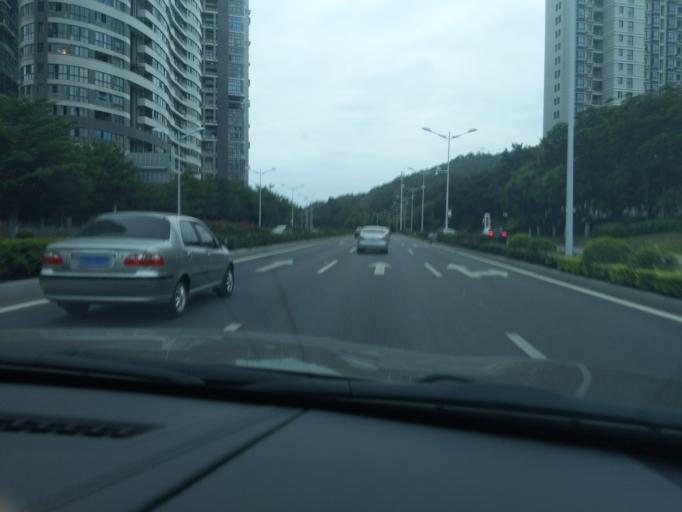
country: CN
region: Fujian
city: Liuwudian
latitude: 24.5007
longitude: 118.1834
